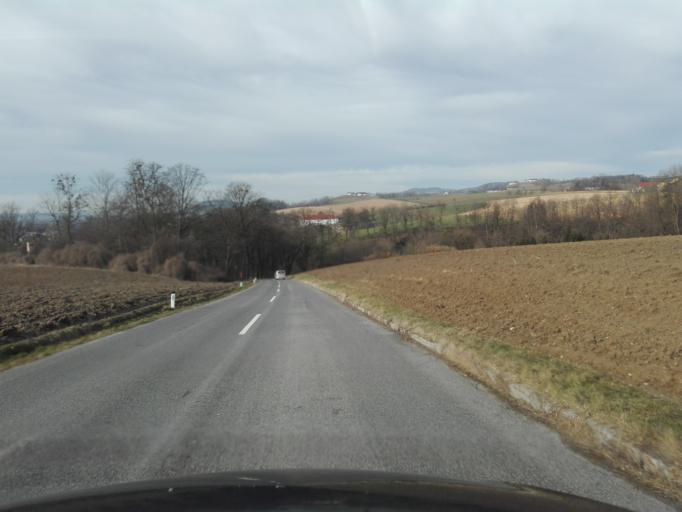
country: AT
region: Lower Austria
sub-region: Politischer Bezirk Amstetten
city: Ennsdorf
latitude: 48.2541
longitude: 14.4957
